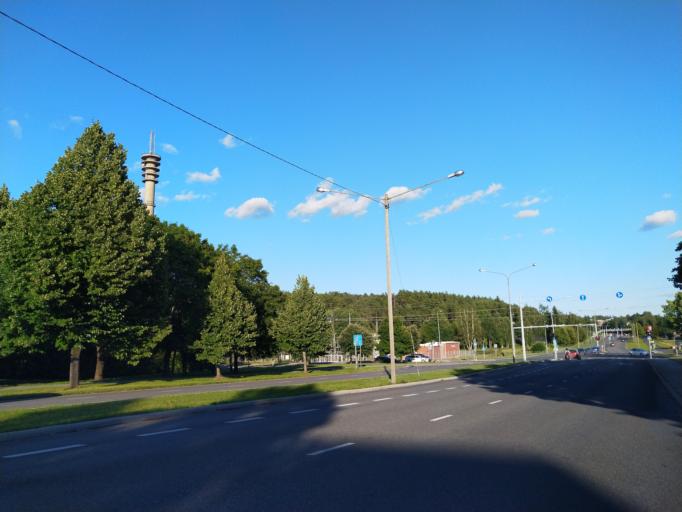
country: FI
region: Varsinais-Suomi
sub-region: Turku
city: Turku
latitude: 60.4463
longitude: 22.3253
